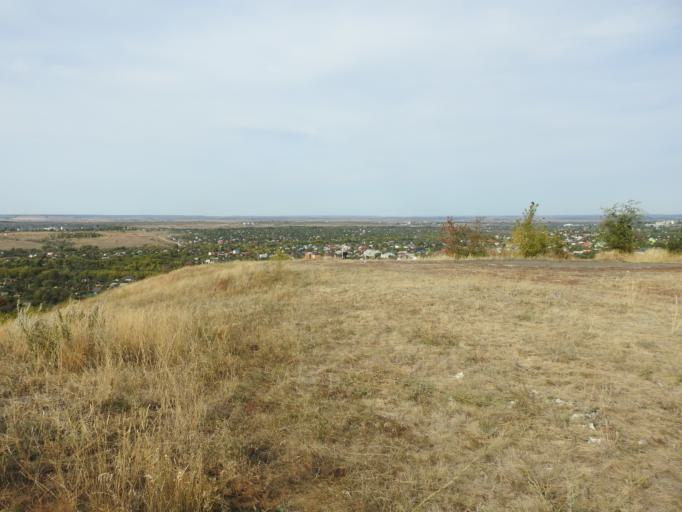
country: RU
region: Saratov
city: Sokolovyy
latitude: 51.5687
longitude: 45.8767
